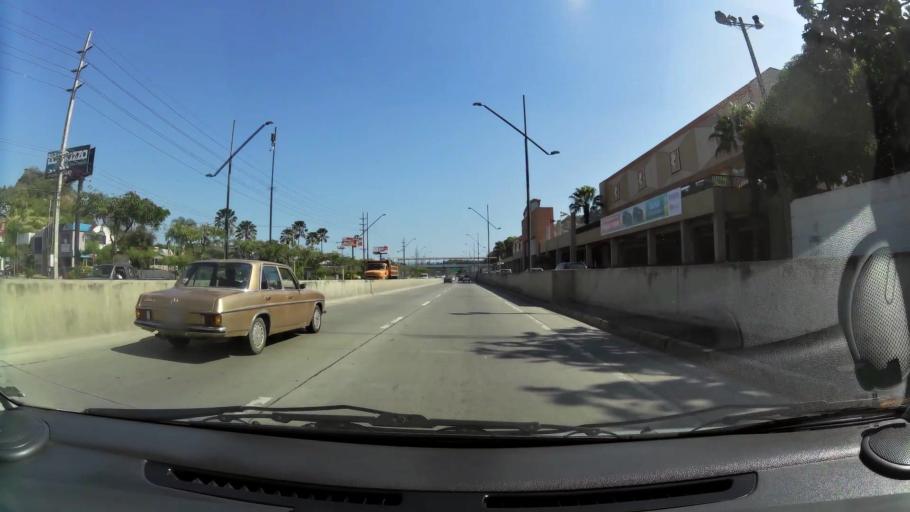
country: EC
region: Guayas
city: Guayaquil
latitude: -2.1758
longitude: -79.9425
